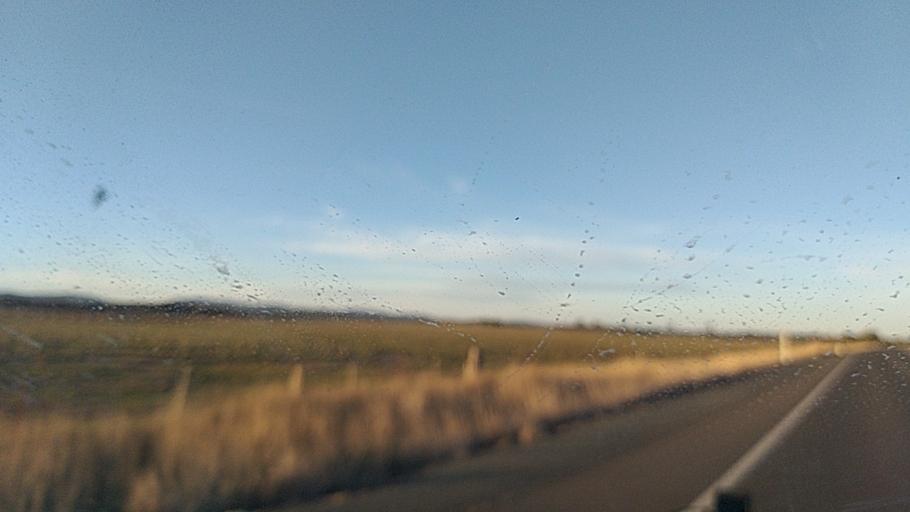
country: AU
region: New South Wales
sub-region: Goulburn Mulwaree
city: Goulburn
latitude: -34.8581
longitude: 149.5510
